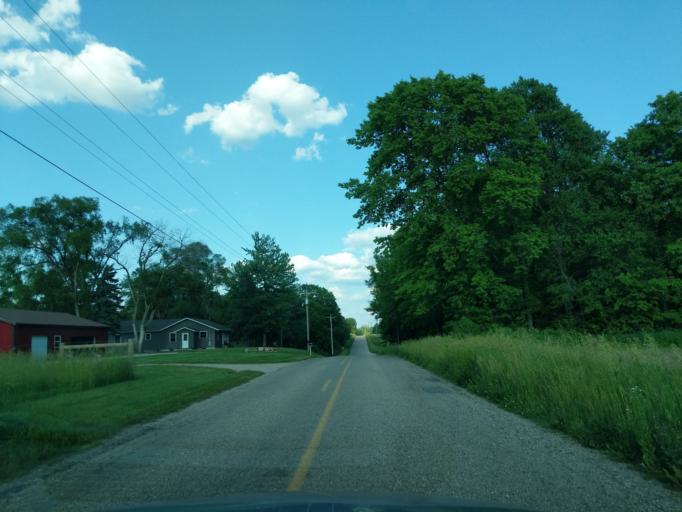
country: US
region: Indiana
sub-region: Kosciusko County
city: North Webster
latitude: 41.3025
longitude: -85.6011
